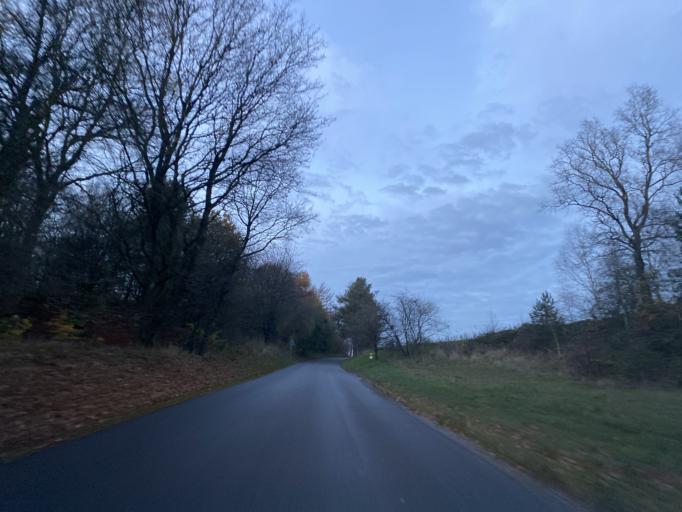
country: DK
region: Central Jutland
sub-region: Silkeborg Kommune
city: Svejbaek
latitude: 56.1601
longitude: 9.6925
